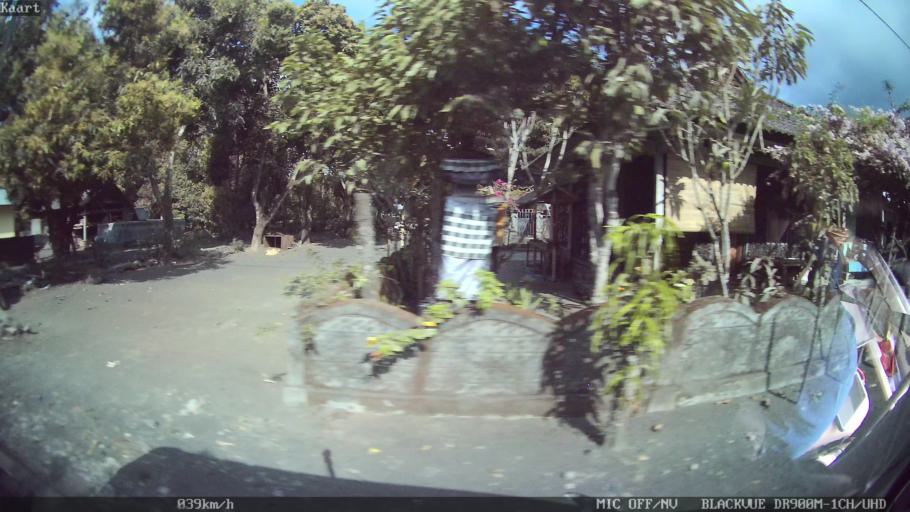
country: ID
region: Bali
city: Banjar Kedisan
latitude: -8.2197
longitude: 115.3635
